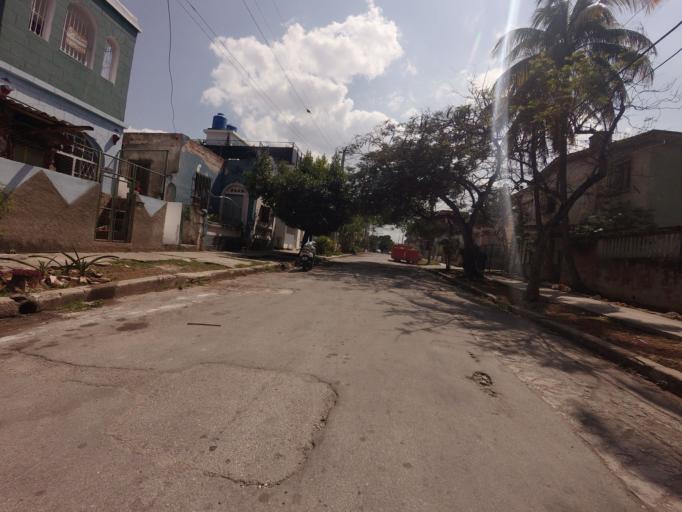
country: CU
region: La Habana
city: Havana
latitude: 23.1140
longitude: -82.4243
